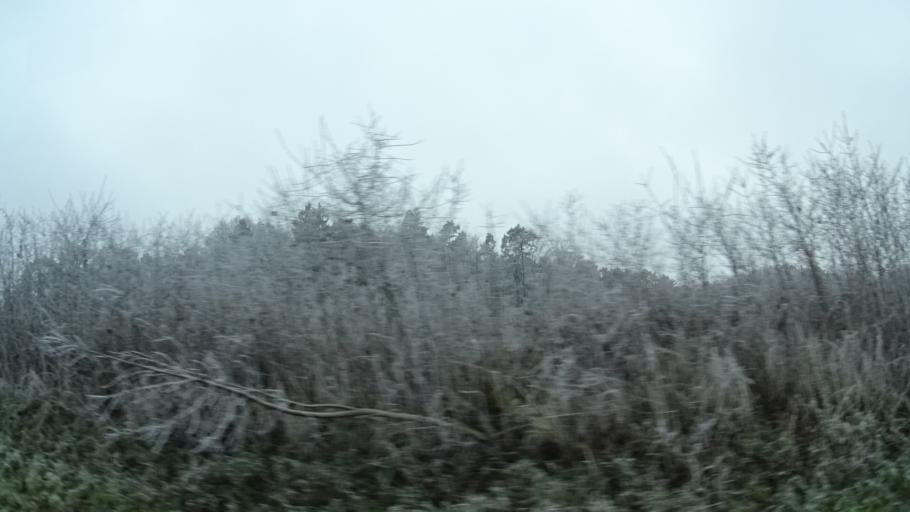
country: DE
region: Baden-Wuerttemberg
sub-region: Regierungsbezirk Stuttgart
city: Boxberg
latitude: 49.5030
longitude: 9.6311
